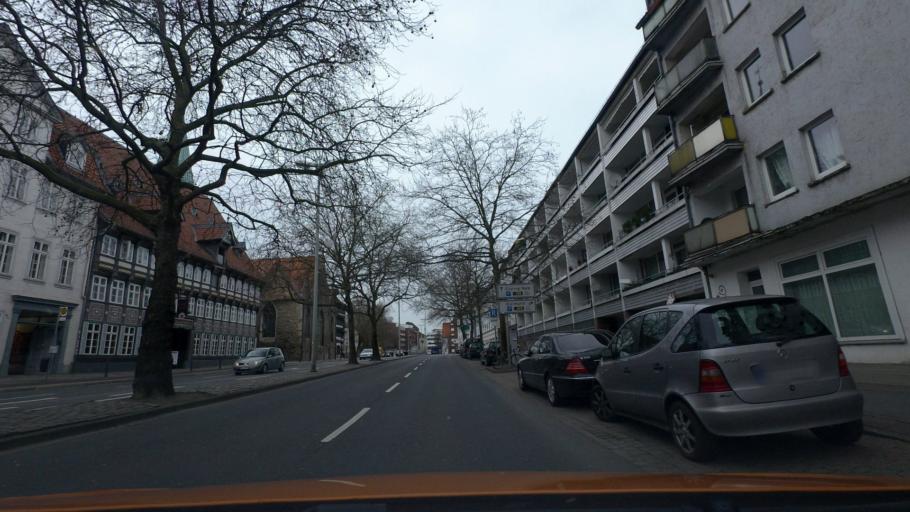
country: DE
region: Lower Saxony
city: Braunschweig
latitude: 52.2601
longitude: 10.5158
